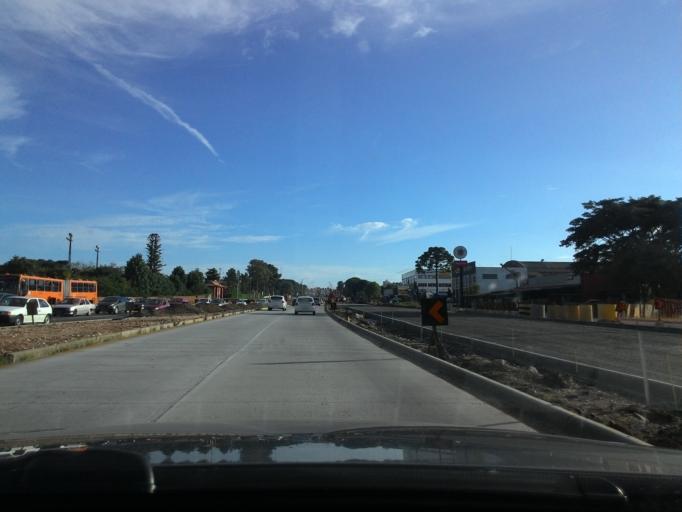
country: BR
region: Parana
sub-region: Pinhais
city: Pinhais
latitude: -25.4218
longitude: -49.2256
